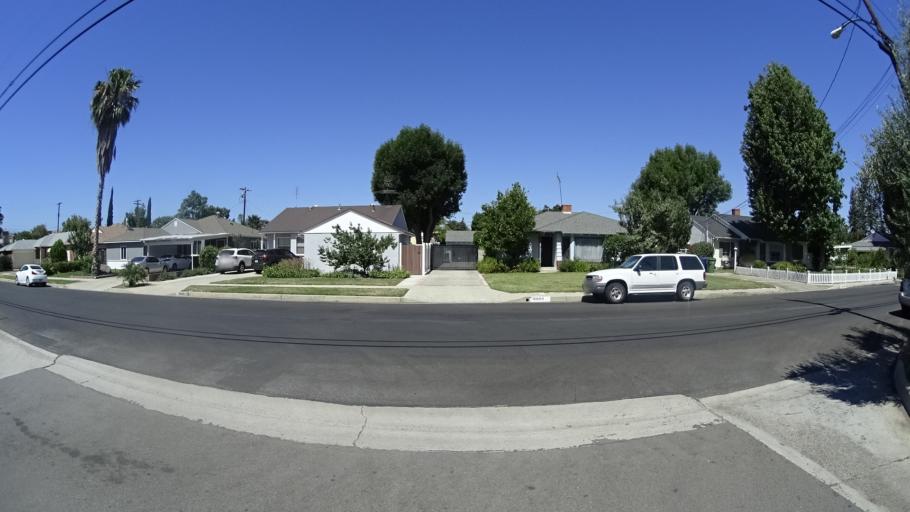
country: US
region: California
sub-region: Los Angeles County
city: Northridge
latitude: 34.1957
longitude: -118.4988
